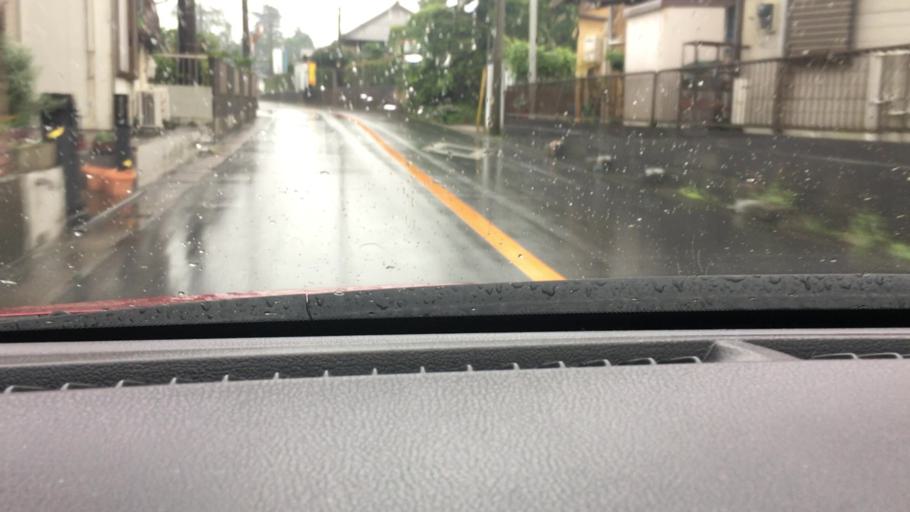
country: JP
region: Chiba
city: Kisarazu
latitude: 35.3726
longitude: 139.9414
